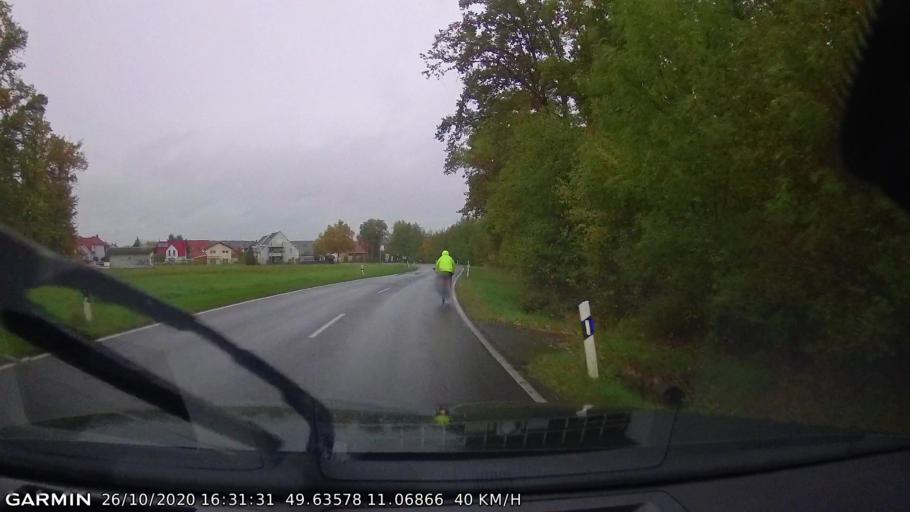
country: DE
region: Bavaria
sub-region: Upper Franconia
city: Langensendelbach
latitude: 49.6358
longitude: 11.0688
